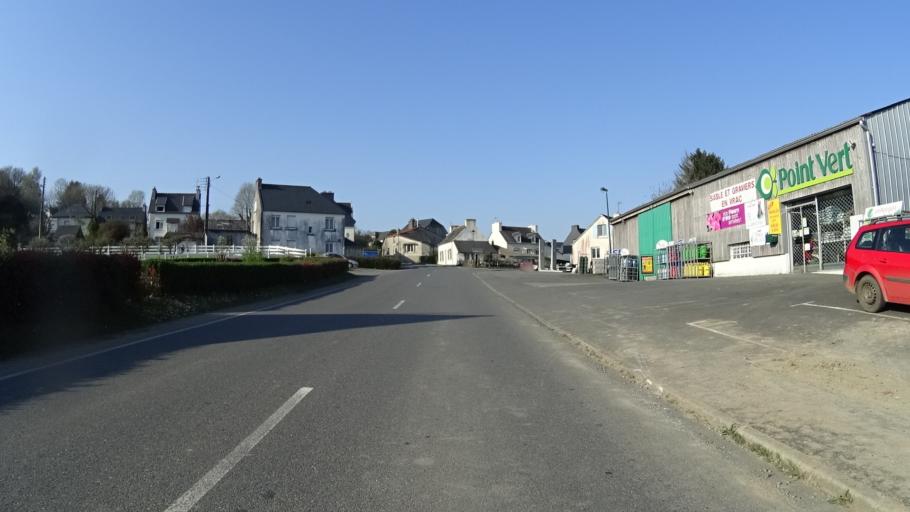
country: FR
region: Brittany
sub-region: Departement du Finistere
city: Sizun
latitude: 48.4021
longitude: -4.0785
